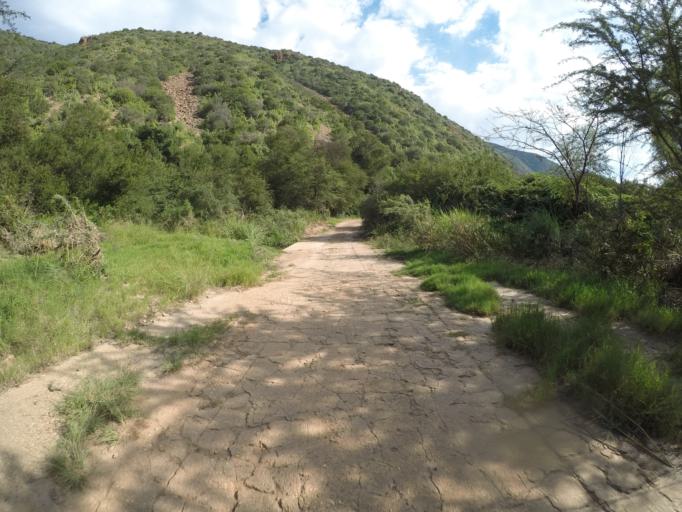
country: ZA
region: Eastern Cape
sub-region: Cacadu District Municipality
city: Kareedouw
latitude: -33.6427
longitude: 24.3165
